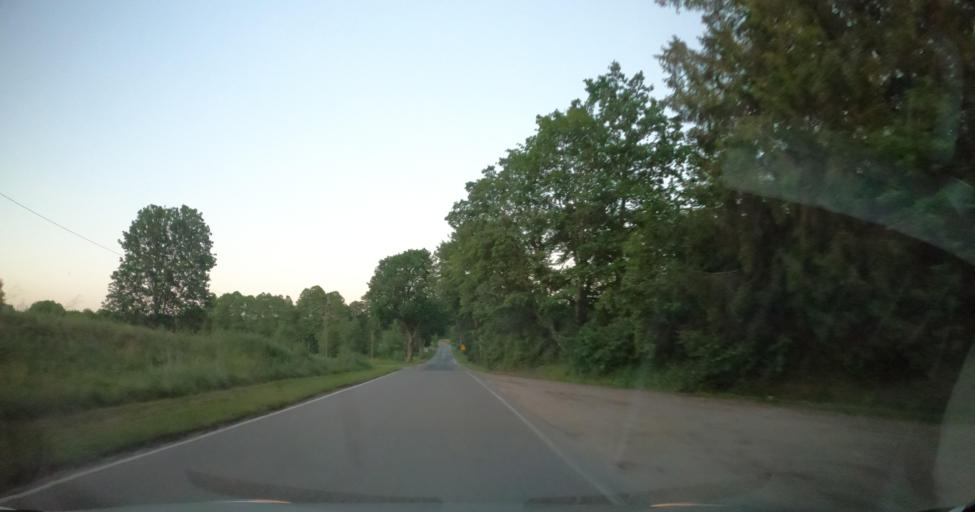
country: PL
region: Pomeranian Voivodeship
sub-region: Powiat wejherowski
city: Luzino
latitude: 54.4667
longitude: 18.0963
